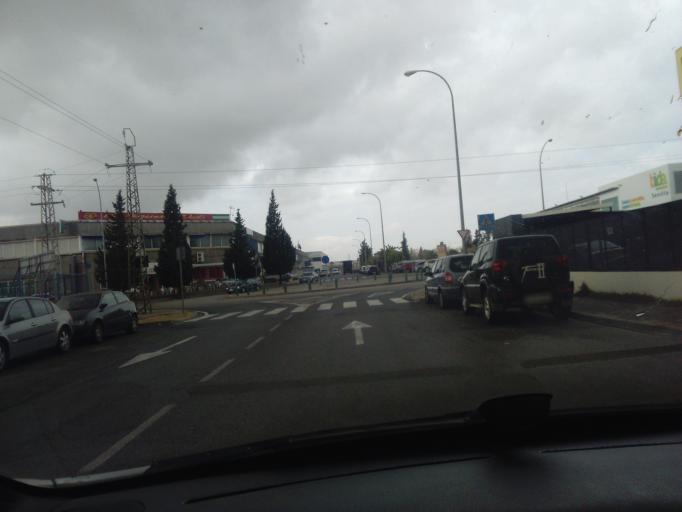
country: ES
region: Andalusia
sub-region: Provincia de Sevilla
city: Sevilla
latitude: 37.3772
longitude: -5.9256
